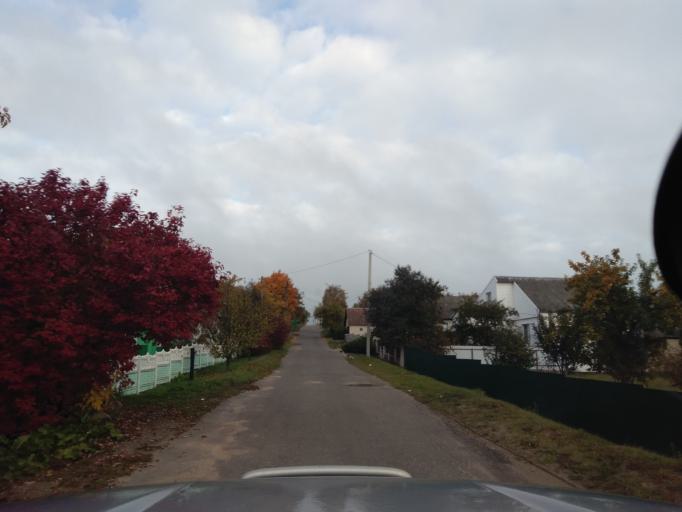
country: BY
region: Minsk
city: Kapyl'
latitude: 53.1572
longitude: 27.0854
